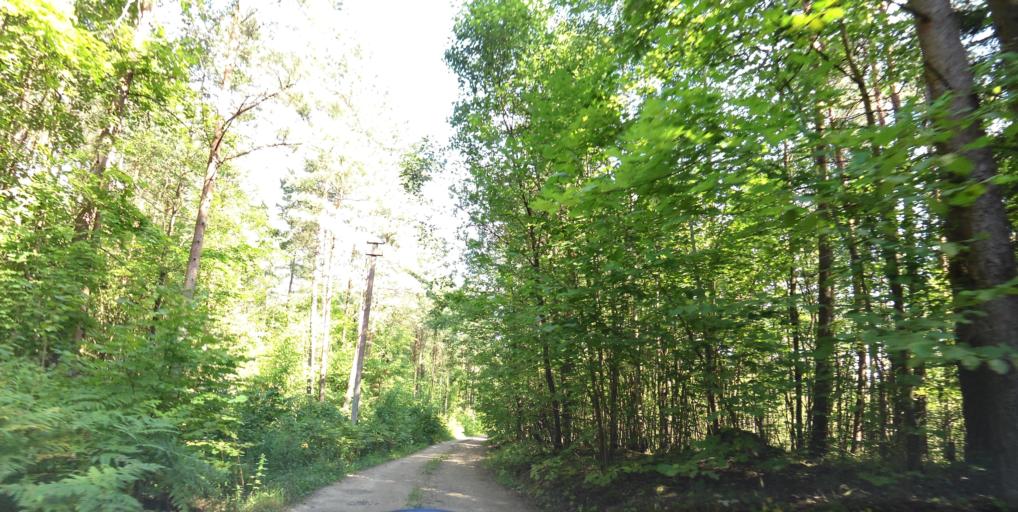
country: LT
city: Grigiskes
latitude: 54.7443
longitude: 25.0229
